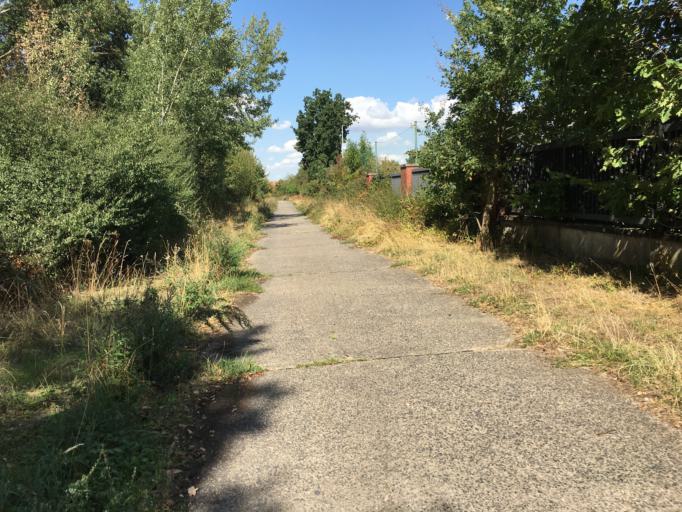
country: DE
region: North Rhine-Westphalia
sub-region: Regierungsbezirk Koln
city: Dueren
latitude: 50.7827
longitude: 6.5019
